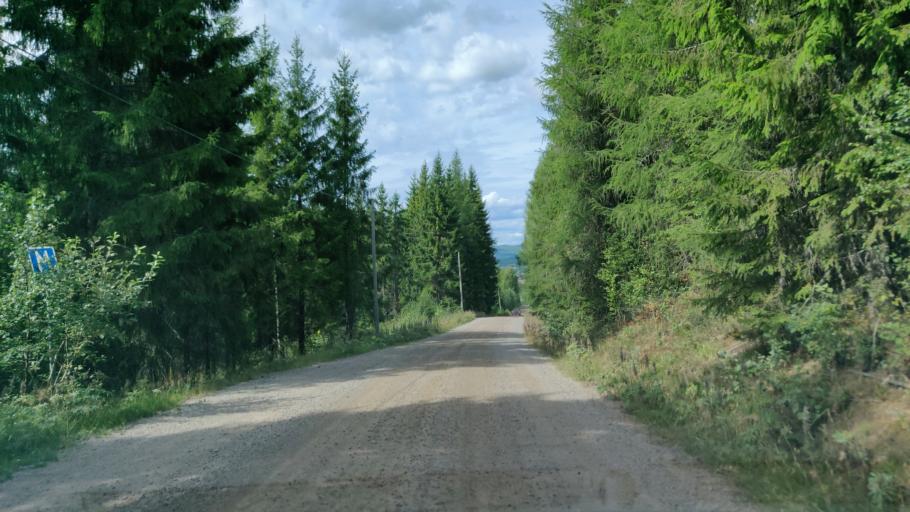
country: SE
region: Vaermland
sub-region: Hagfors Kommun
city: Hagfors
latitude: 60.0165
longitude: 13.7033
